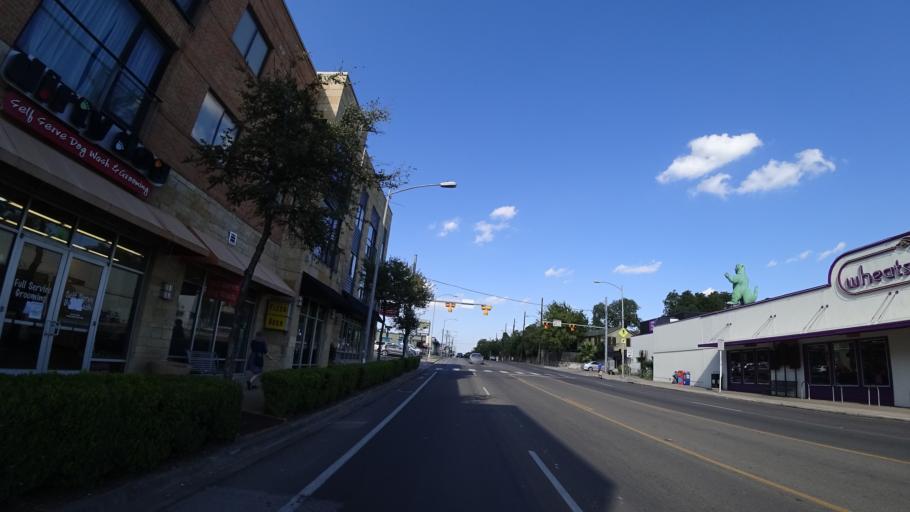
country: US
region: Texas
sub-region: Travis County
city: Austin
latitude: 30.2976
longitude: -97.7415
